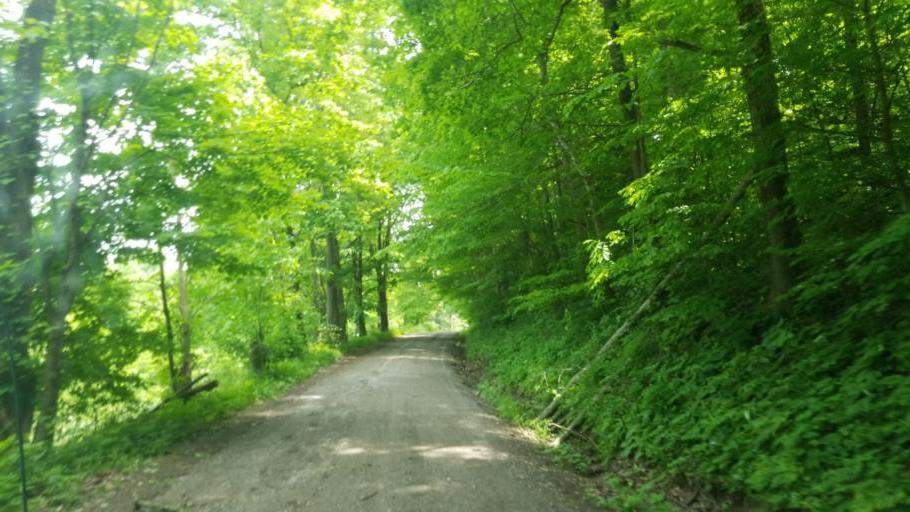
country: US
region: Ohio
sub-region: Holmes County
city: Millersburg
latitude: 40.4838
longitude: -81.8078
